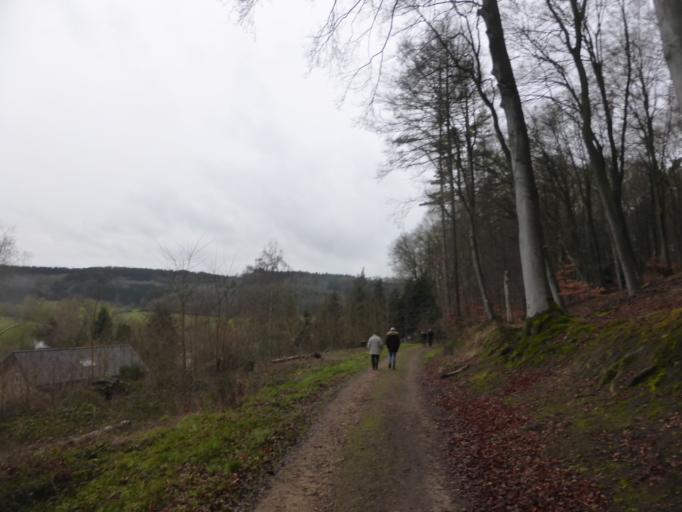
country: LU
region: Luxembourg
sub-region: Canton de Mersch
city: Lintgen
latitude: 49.7231
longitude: 6.1452
